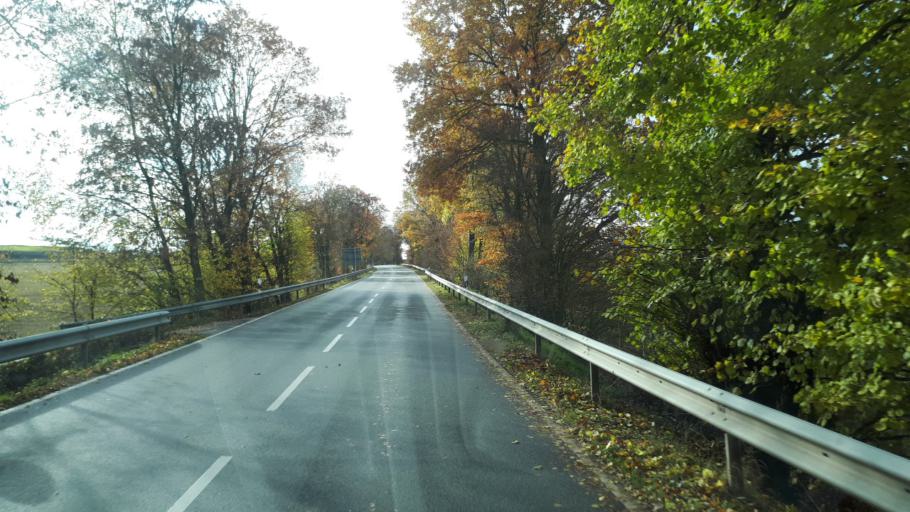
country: DE
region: Rheinland-Pfalz
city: Alflen
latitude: 50.1830
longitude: 7.0559
